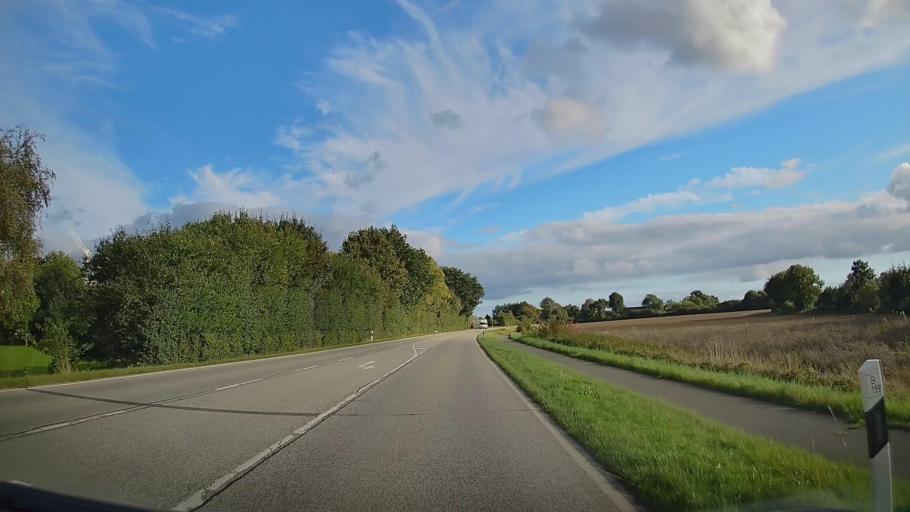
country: DE
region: Schleswig-Holstein
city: Nieby
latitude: 54.7351
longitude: 9.9384
